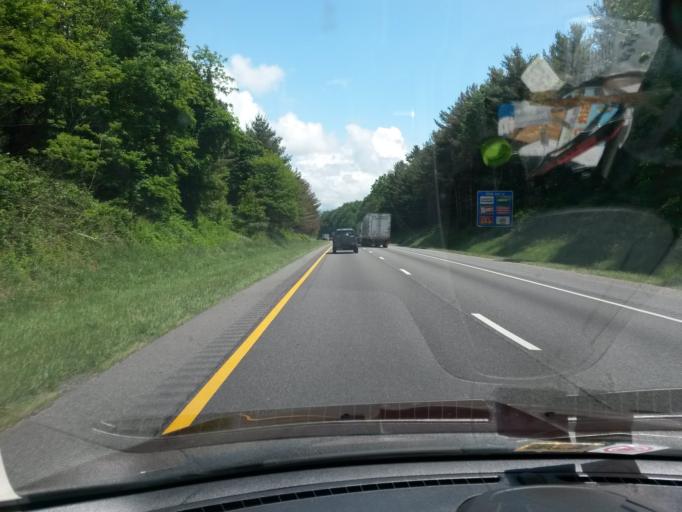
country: US
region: Virginia
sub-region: Carroll County
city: Woodlawn
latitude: 36.7620
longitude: -80.7957
